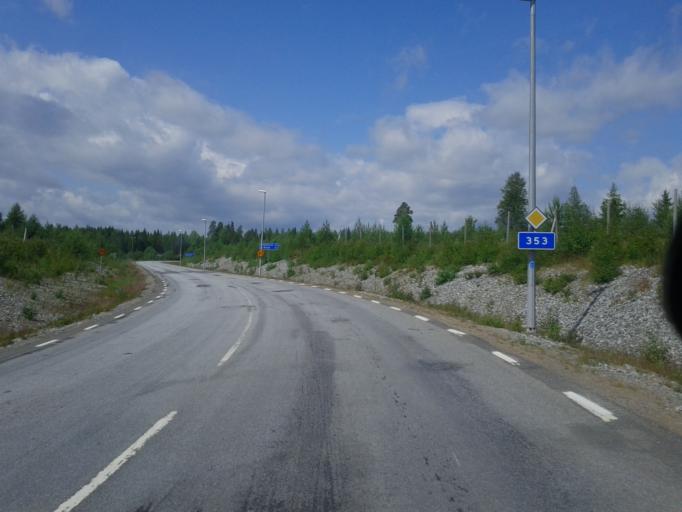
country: SE
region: Vaesterbotten
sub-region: Nordmalings Kommun
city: Nordmaling
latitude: 63.5787
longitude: 19.4619
